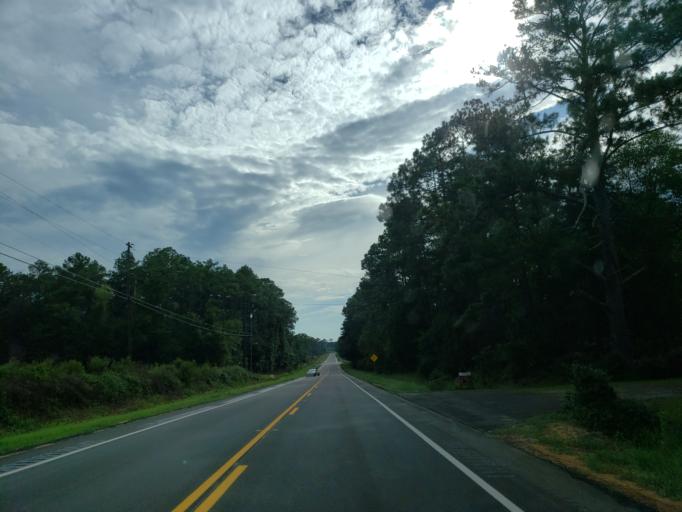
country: US
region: Georgia
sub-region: Irwin County
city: Ocilla
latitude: 31.5655
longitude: -83.3159
